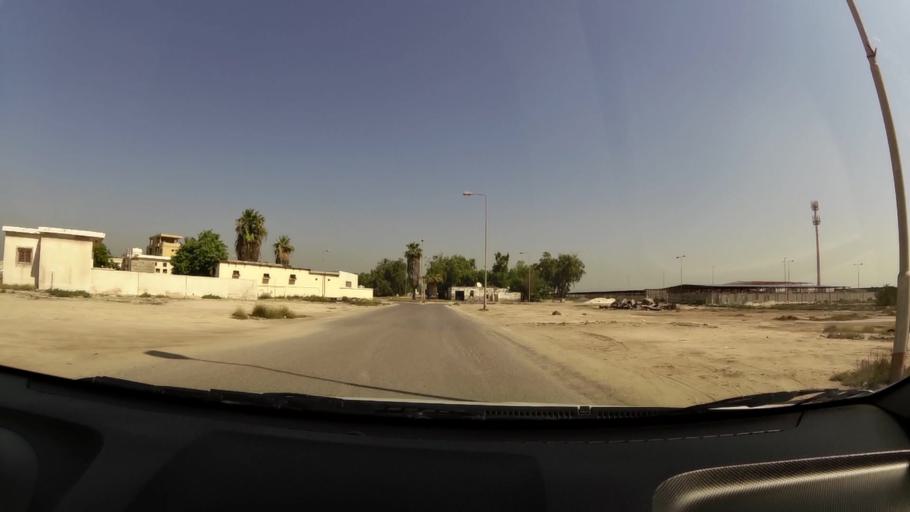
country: AE
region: Umm al Qaywayn
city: Umm al Qaywayn
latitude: 25.5861
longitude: 55.5783
